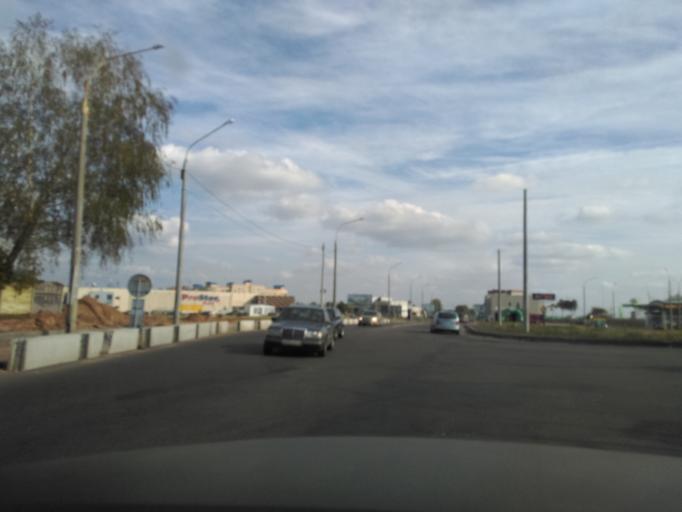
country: BY
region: Minsk
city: Machulishchy
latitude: 53.8358
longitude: 27.6008
